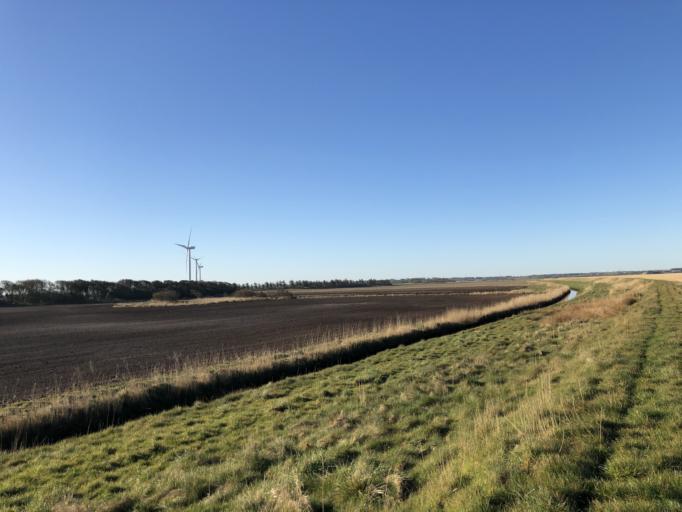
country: DK
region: Central Jutland
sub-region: Holstebro Kommune
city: Ulfborg
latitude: 56.3090
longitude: 8.2936
